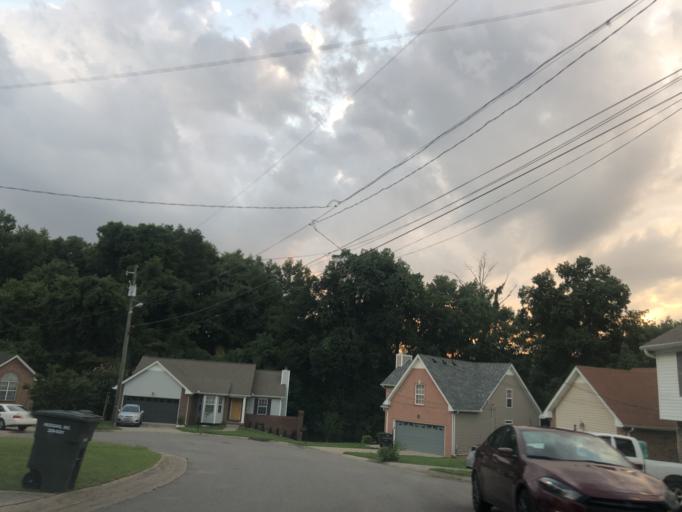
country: US
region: Tennessee
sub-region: Davidson County
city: Lakewood
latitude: 36.1467
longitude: -86.6387
